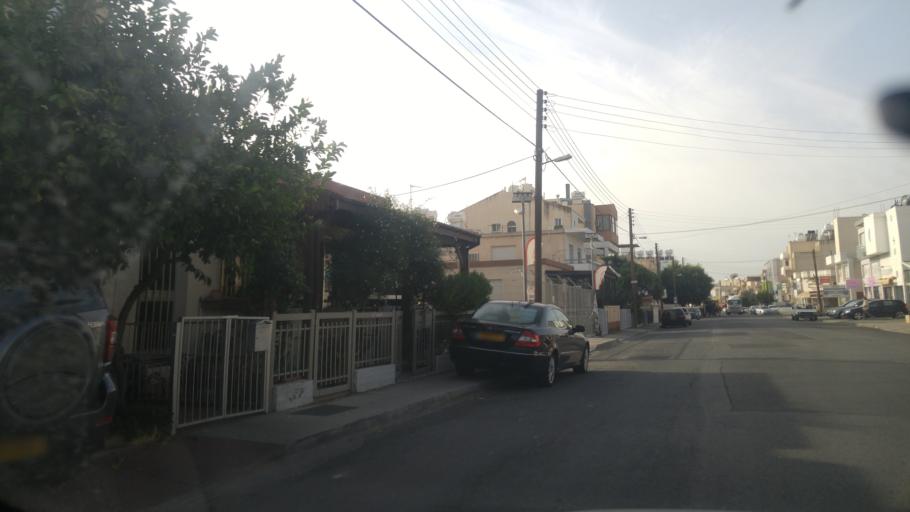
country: CY
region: Limassol
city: Limassol
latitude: 34.6715
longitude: 33.0057
